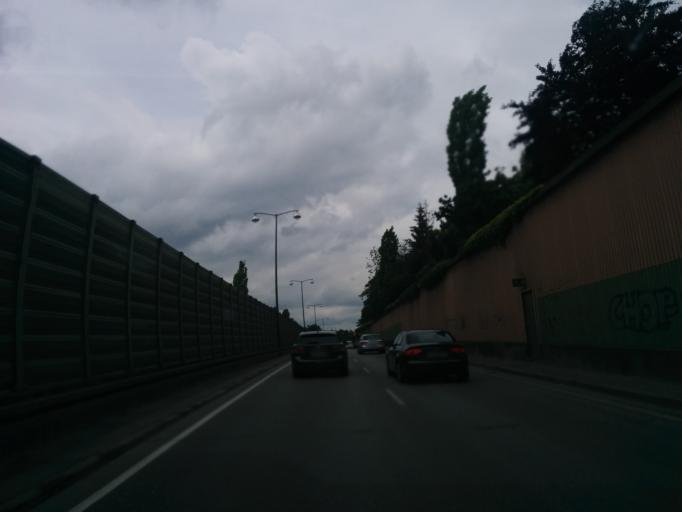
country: DE
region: Bavaria
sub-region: Swabia
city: Stadtbergen
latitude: 48.3680
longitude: 10.8548
